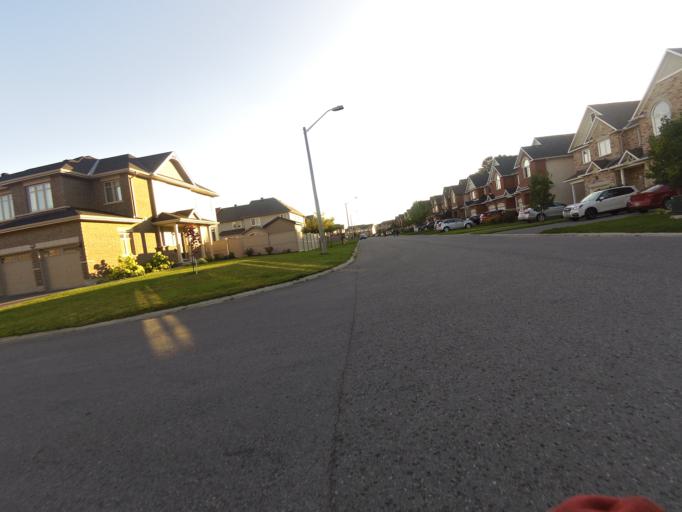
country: CA
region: Ontario
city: Bells Corners
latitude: 45.3638
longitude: -75.9298
